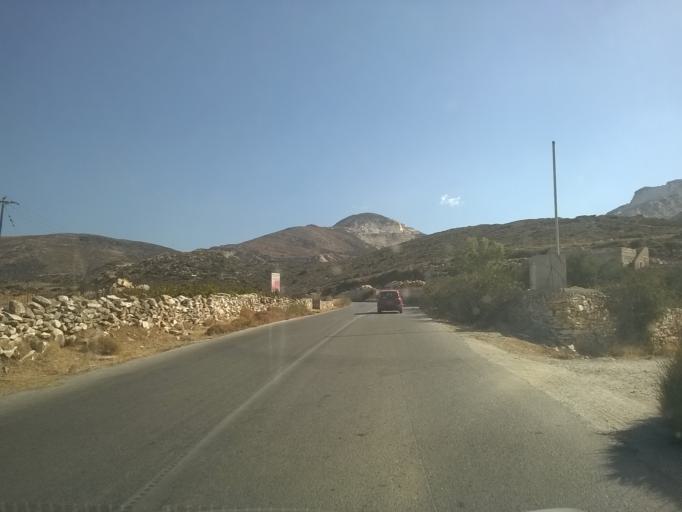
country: GR
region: South Aegean
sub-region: Nomos Kykladon
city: Filotion
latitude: 37.0879
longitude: 25.4530
